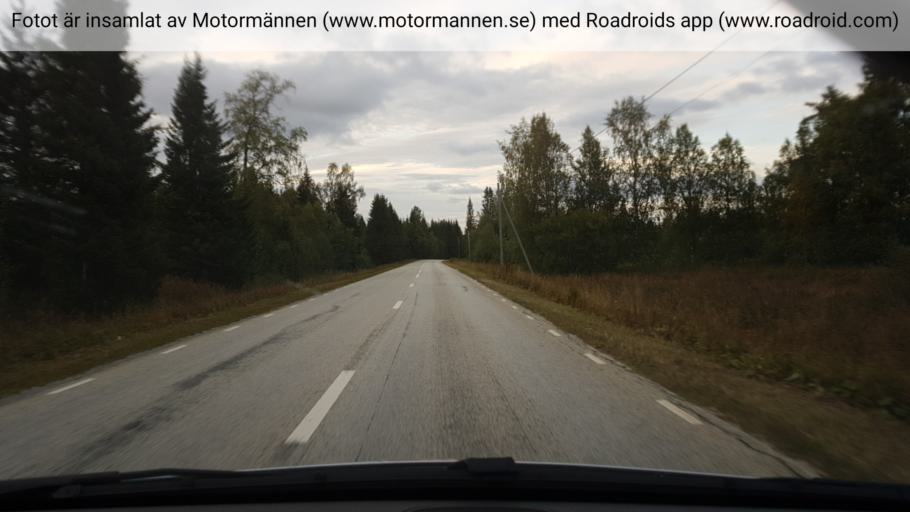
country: SE
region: Jaemtland
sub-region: Bergs Kommun
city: Hoverberg
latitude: 62.5976
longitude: 14.3123
